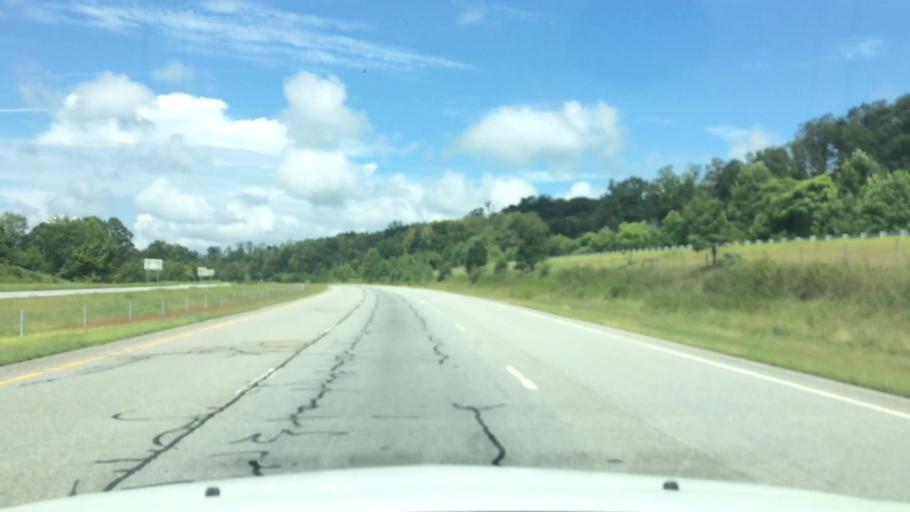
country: US
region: North Carolina
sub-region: Yadkin County
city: Jonesville
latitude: 36.1452
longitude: -80.8991
